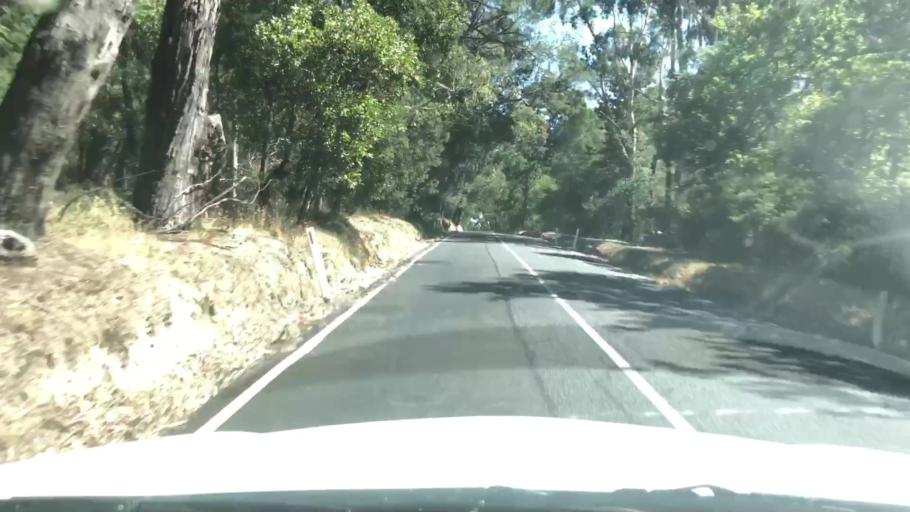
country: AU
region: Victoria
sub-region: Yarra Ranges
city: Macclesfield
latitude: -37.8288
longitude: 145.4893
